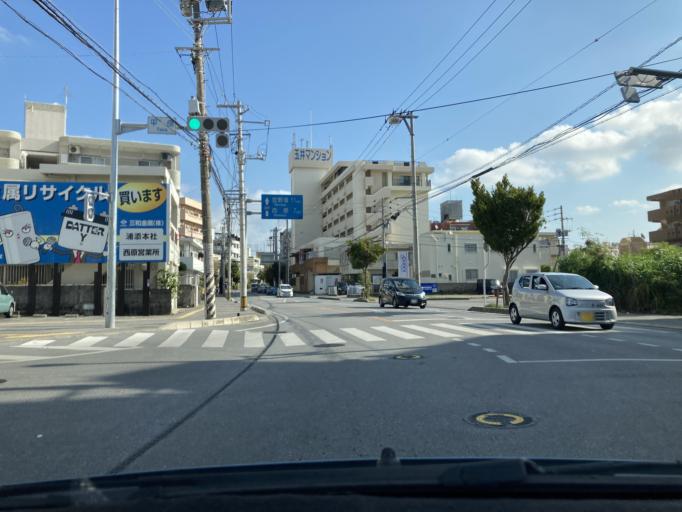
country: JP
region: Okinawa
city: Naha-shi
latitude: 26.2277
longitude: 127.7194
